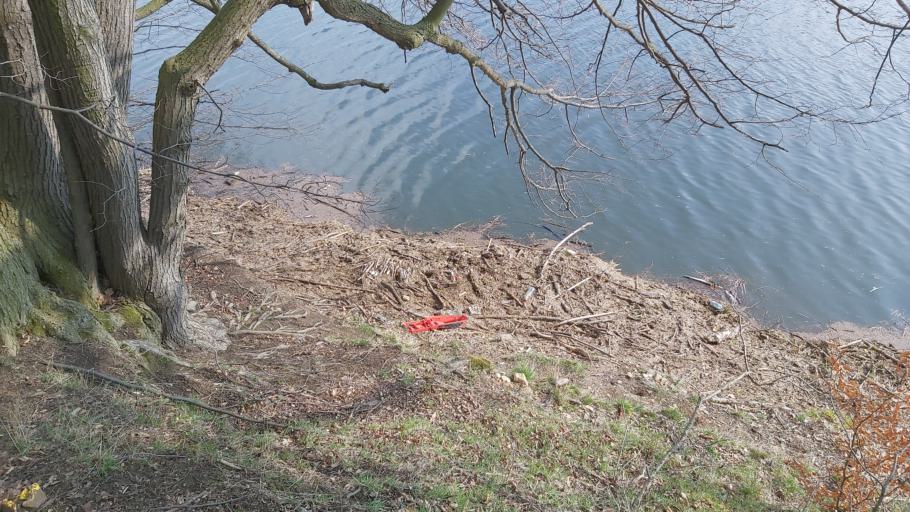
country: PL
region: Lower Silesian Voivodeship
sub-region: Powiat lwowecki
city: Gryfow Slaski
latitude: 51.0322
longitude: 15.3887
